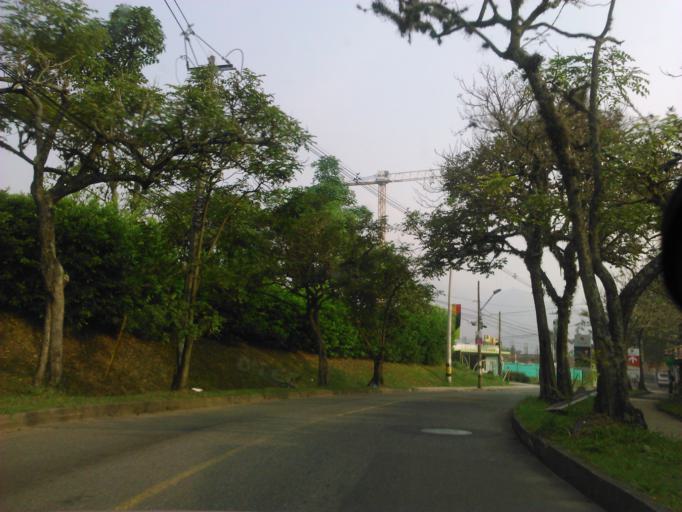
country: CO
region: Antioquia
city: Sabaneta
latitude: 6.1586
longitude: -75.6236
